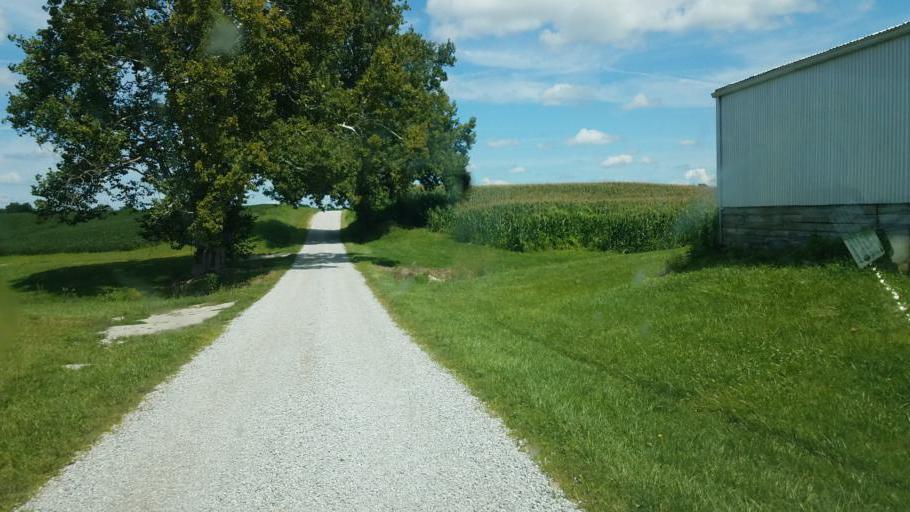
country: US
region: Ohio
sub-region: Delaware County
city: Sunbury
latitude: 40.3188
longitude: -82.8095
